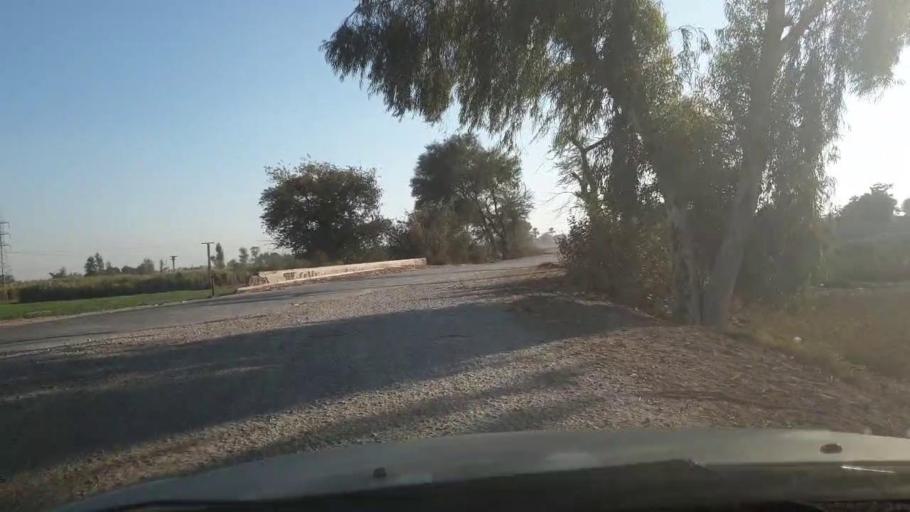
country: PK
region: Sindh
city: Ghotki
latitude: 28.0332
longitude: 69.3232
